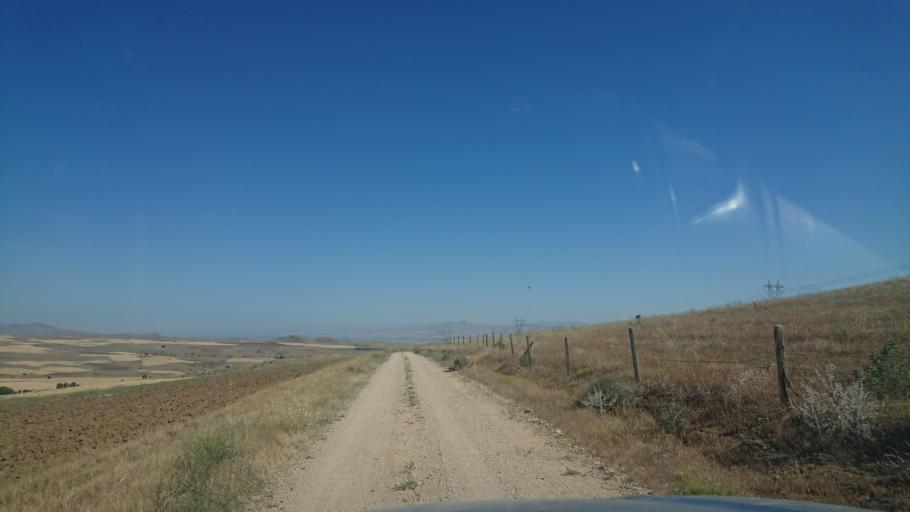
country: TR
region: Aksaray
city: Agacoren
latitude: 38.9167
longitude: 33.8929
